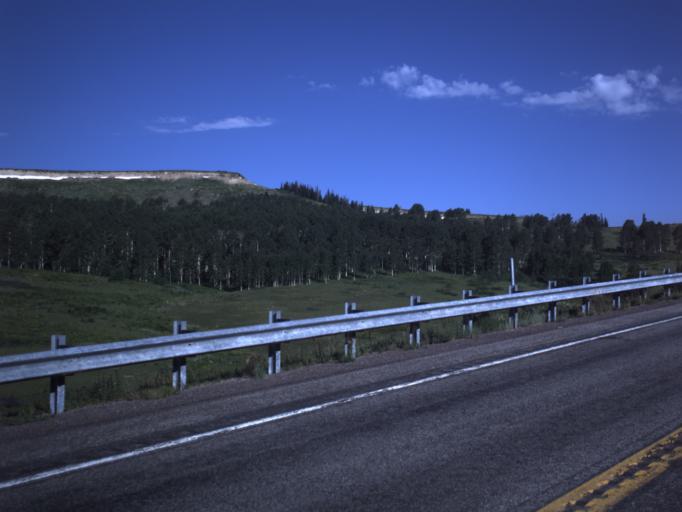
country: US
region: Utah
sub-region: Sanpete County
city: Fairview
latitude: 39.6085
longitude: -111.2797
